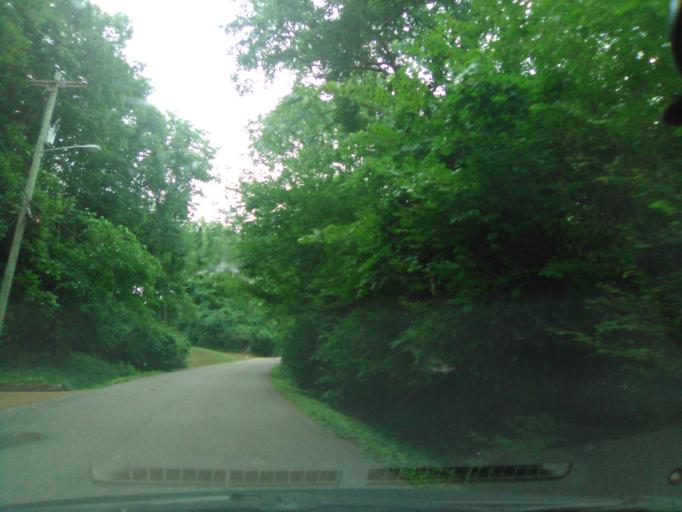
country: US
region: Tennessee
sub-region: Davidson County
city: Belle Meade
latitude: 36.1029
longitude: -86.8888
